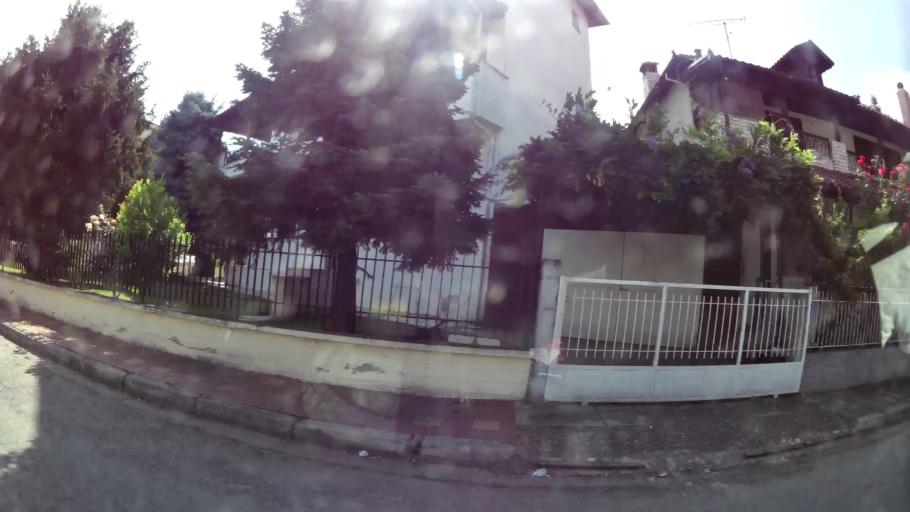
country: GR
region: Central Macedonia
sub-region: Nomos Pierias
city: Katerini
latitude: 40.2808
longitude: 22.5021
